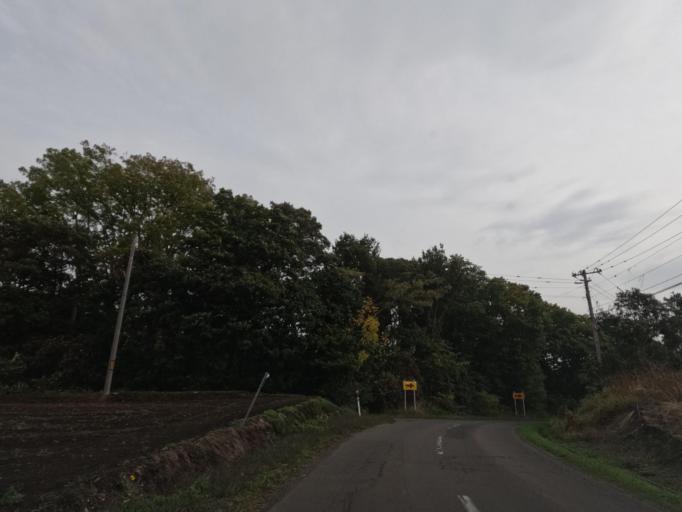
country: JP
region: Hokkaido
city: Date
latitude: 42.4171
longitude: 140.9146
